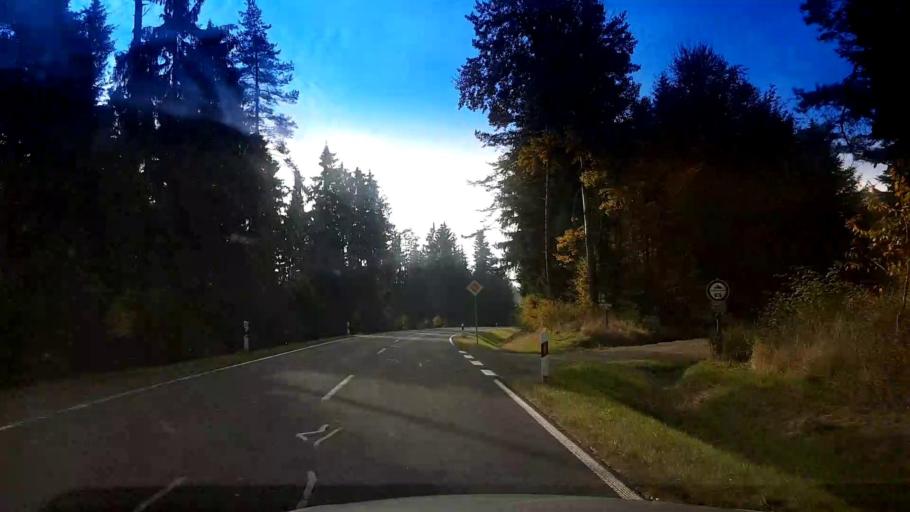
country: DE
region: Bavaria
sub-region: Upper Franconia
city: Schirnding
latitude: 50.0633
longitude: 12.2489
